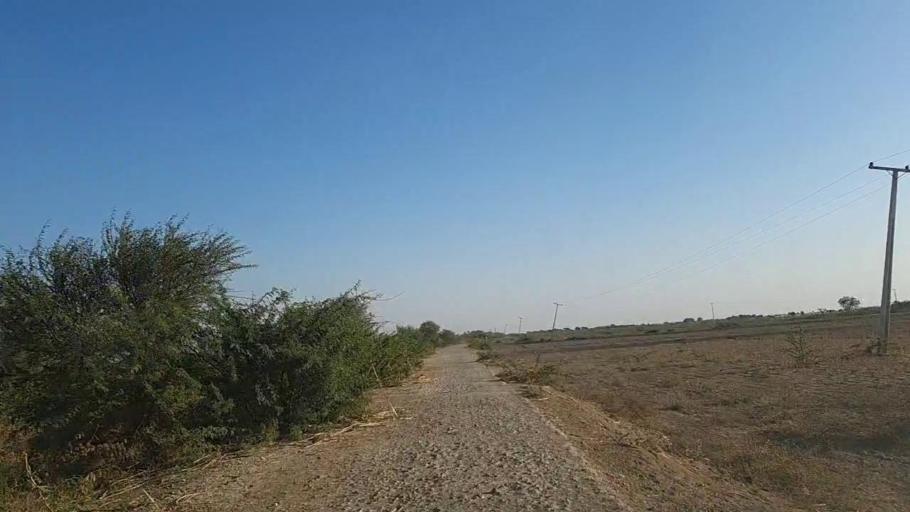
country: PK
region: Sindh
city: Naukot
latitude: 24.9858
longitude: 69.3859
